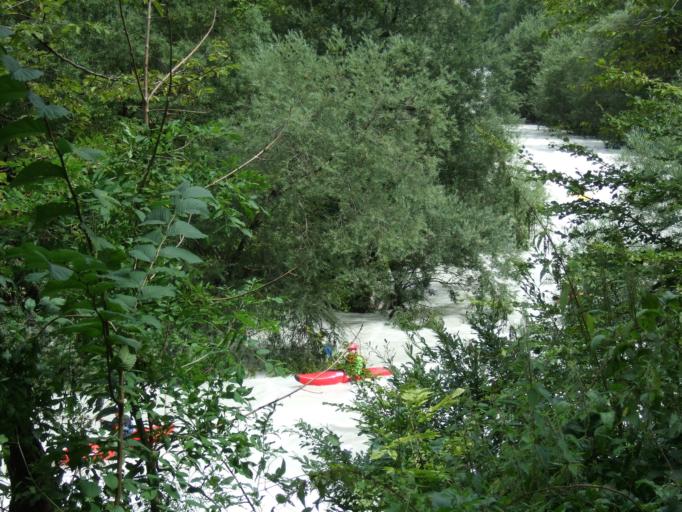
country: SI
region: Bovec
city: Bovec
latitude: 46.3332
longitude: 13.5963
